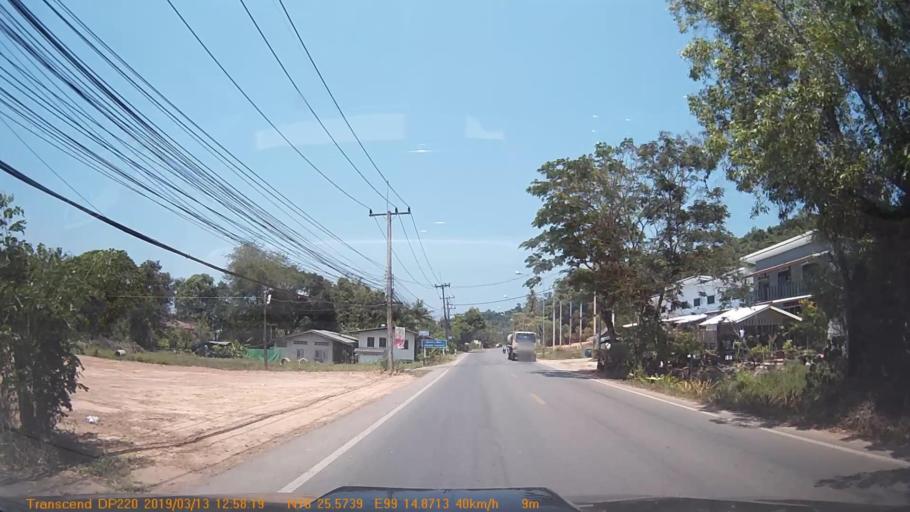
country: TH
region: Chumphon
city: Chumphon
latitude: 10.4265
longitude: 99.2479
